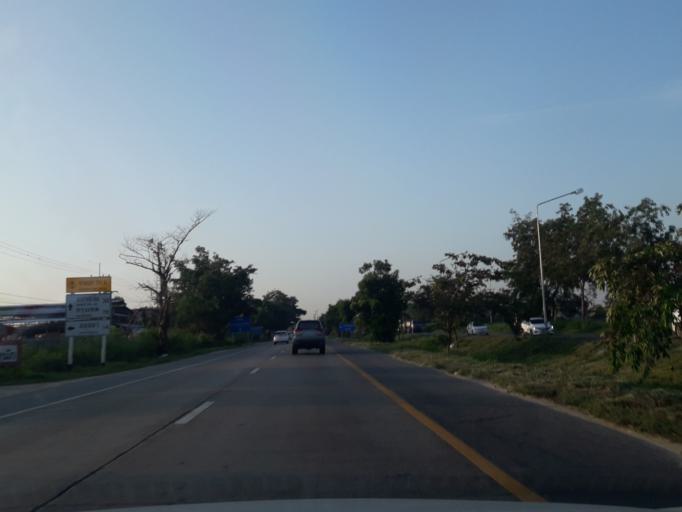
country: TH
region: Phra Nakhon Si Ayutthaya
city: Phra Nakhon Si Ayutthaya
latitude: 14.3153
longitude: 100.5273
